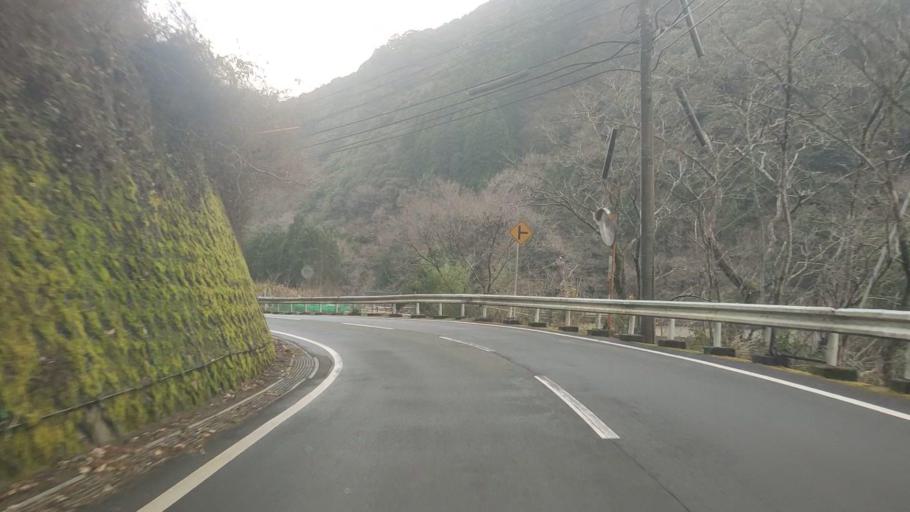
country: JP
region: Kumamoto
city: Hitoyoshi
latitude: 32.4304
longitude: 130.8589
